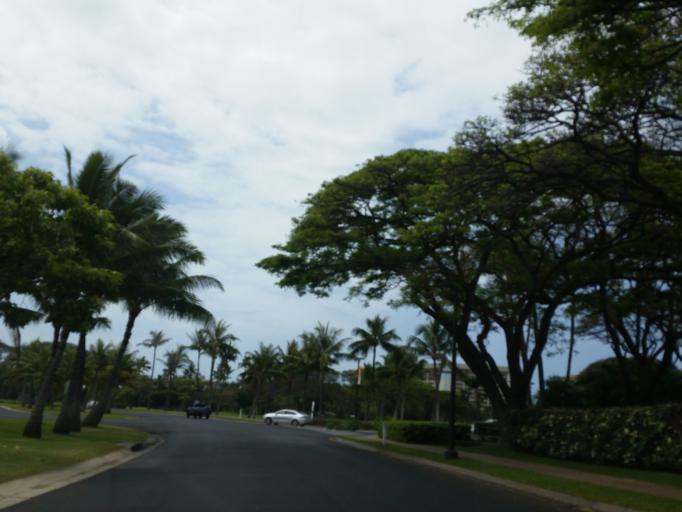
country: US
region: Hawaii
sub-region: Maui County
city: Ka'anapali
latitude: 20.9193
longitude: -156.6939
